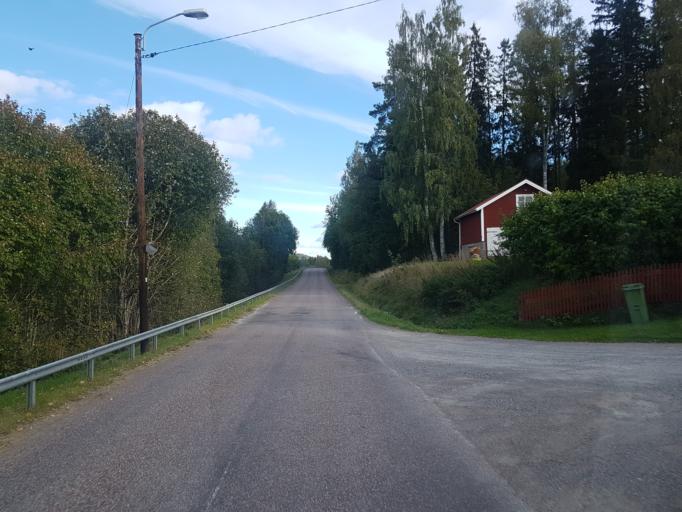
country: SE
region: Dalarna
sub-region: Saters Kommun
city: Saeter
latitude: 60.3638
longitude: 15.7291
